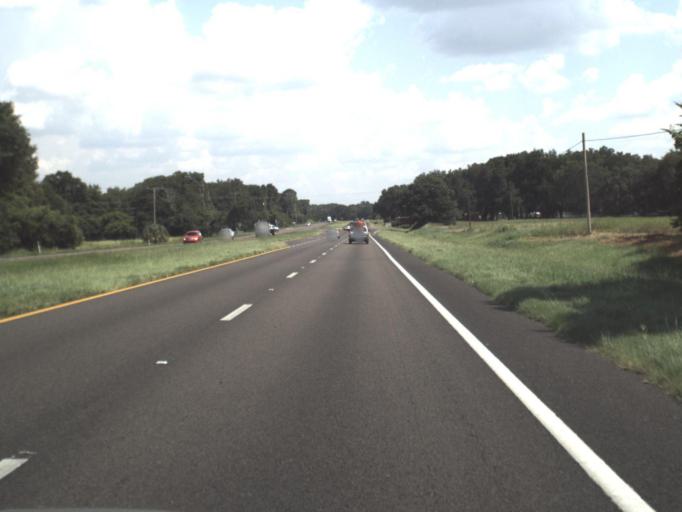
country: US
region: Florida
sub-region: Polk County
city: Willow Oak
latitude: 27.9325
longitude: -82.0824
